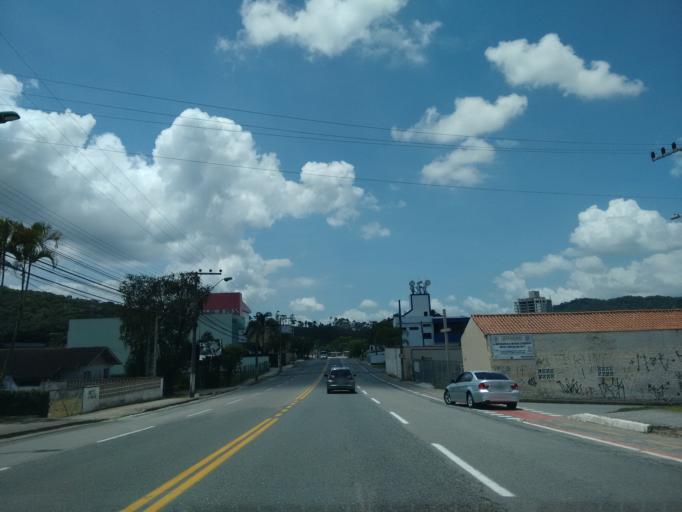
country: BR
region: Santa Catarina
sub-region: Blumenau
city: Blumenau
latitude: -26.9018
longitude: -49.0407
